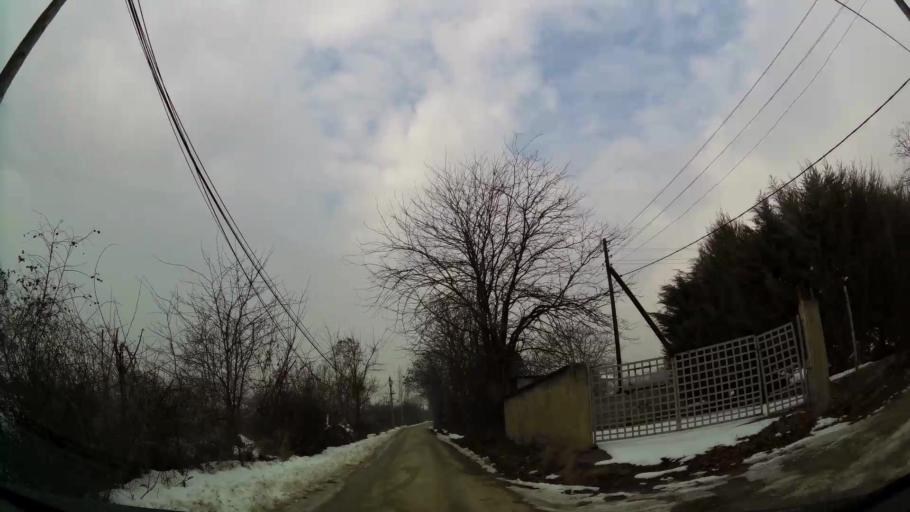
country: MK
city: Kondovo
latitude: 42.0318
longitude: 21.3369
